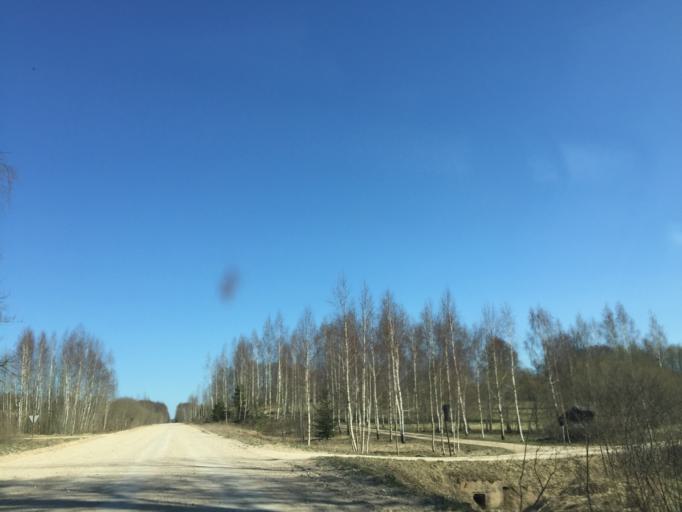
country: LV
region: Malpils
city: Malpils
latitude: 57.0242
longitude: 24.9726
